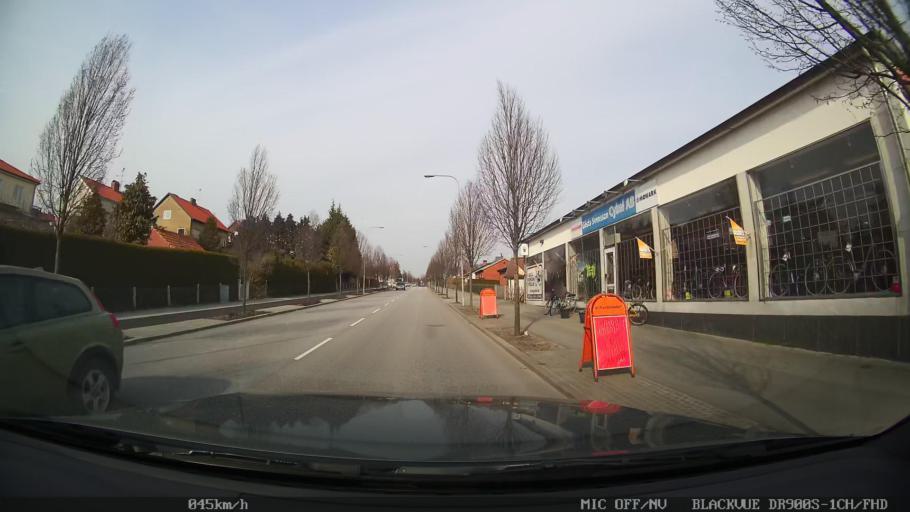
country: SE
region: Skane
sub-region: Ystads Kommun
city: Ystad
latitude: 55.4347
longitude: 13.8217
